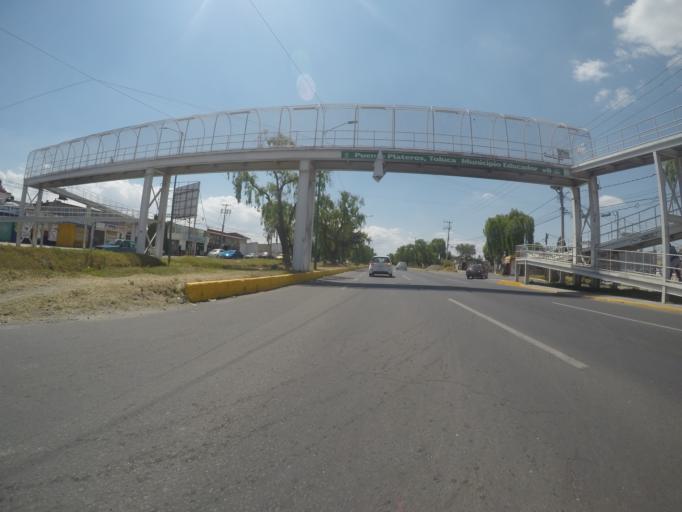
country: MX
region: Mexico
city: San Buenaventura
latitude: 19.2566
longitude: -99.6709
